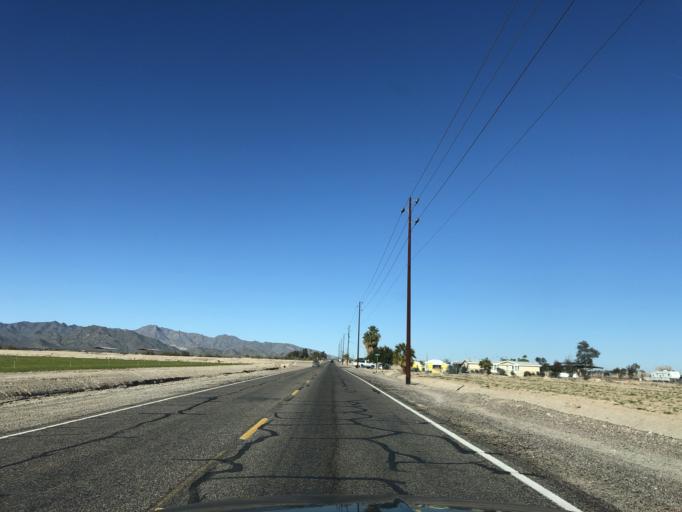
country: US
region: Arizona
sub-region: Maricopa County
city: Buckeye
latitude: 33.4233
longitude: -112.5042
